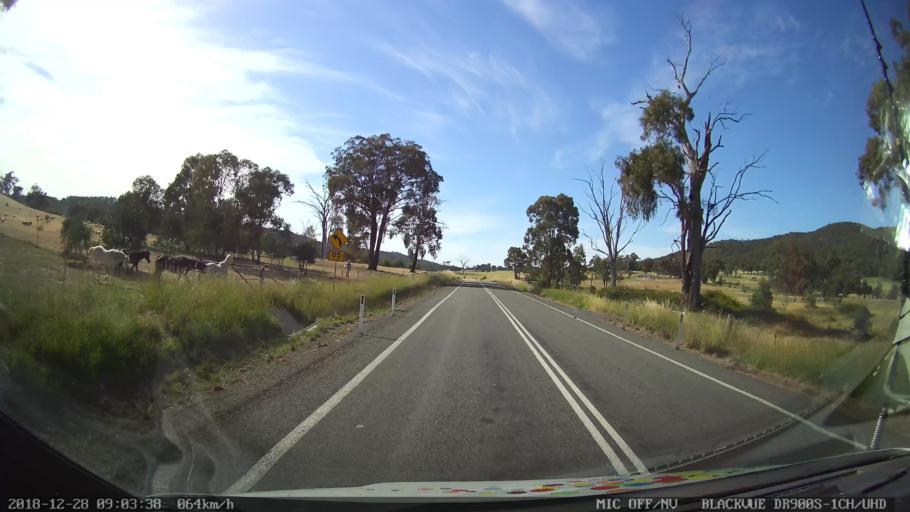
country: AU
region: New South Wales
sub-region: Upper Lachlan Shire
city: Crookwell
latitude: -34.1653
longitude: 149.3384
